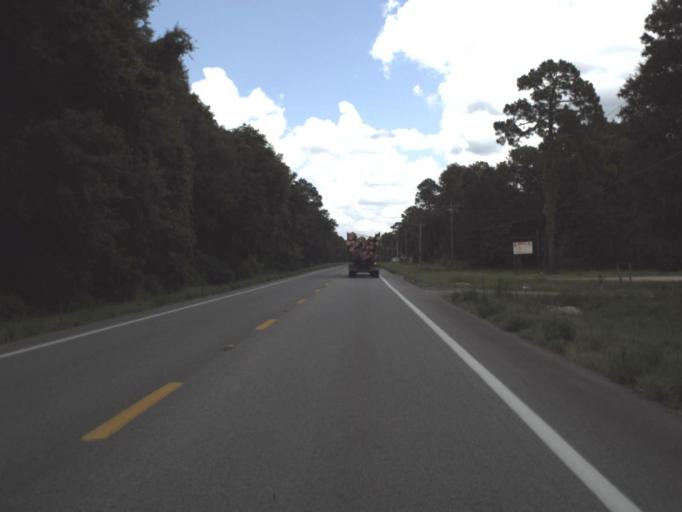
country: US
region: Florida
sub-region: Taylor County
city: Perry
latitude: 30.0959
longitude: -83.6312
